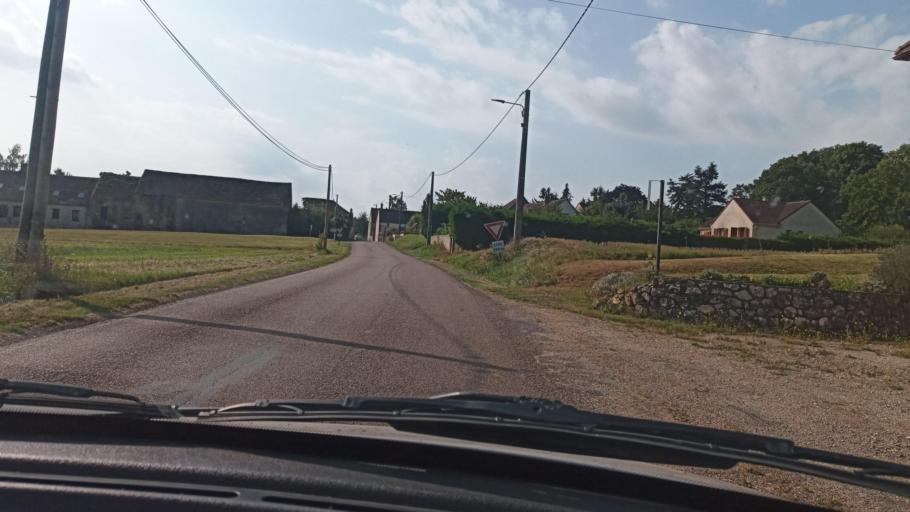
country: FR
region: Bourgogne
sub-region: Departement de l'Yonne
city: Saint-Valerien
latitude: 48.2131
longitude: 3.0718
